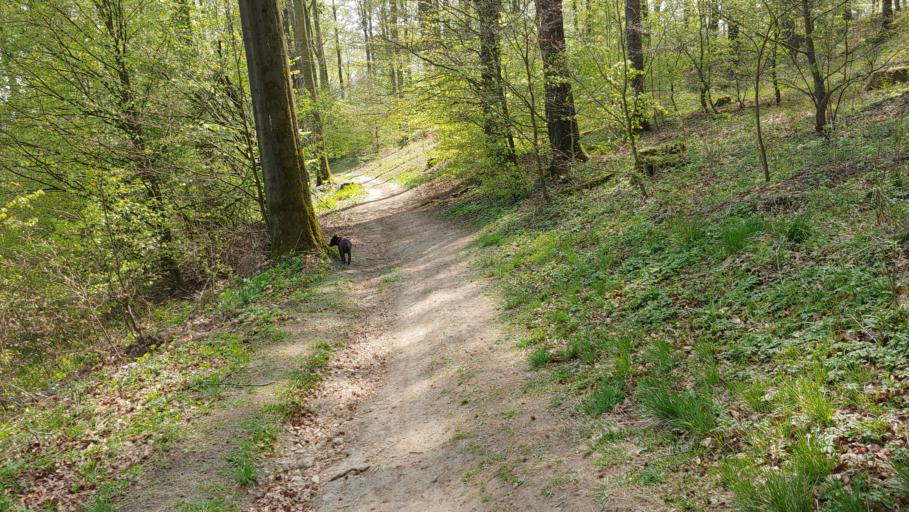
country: DE
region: Hesse
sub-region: Regierungsbezirk Kassel
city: Baunatal
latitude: 51.3054
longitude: 9.3578
